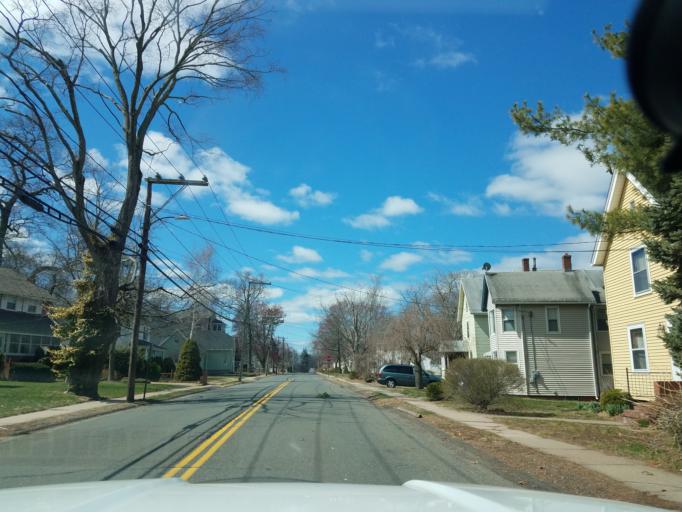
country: US
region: Connecticut
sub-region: Hartford County
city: East Hartford
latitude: 41.7827
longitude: -72.6017
